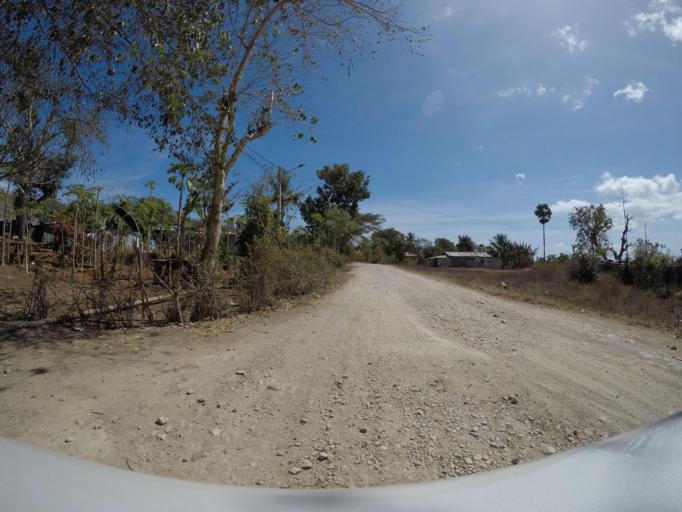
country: TL
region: Baucau
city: Baucau
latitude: -8.4736
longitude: 126.4539
